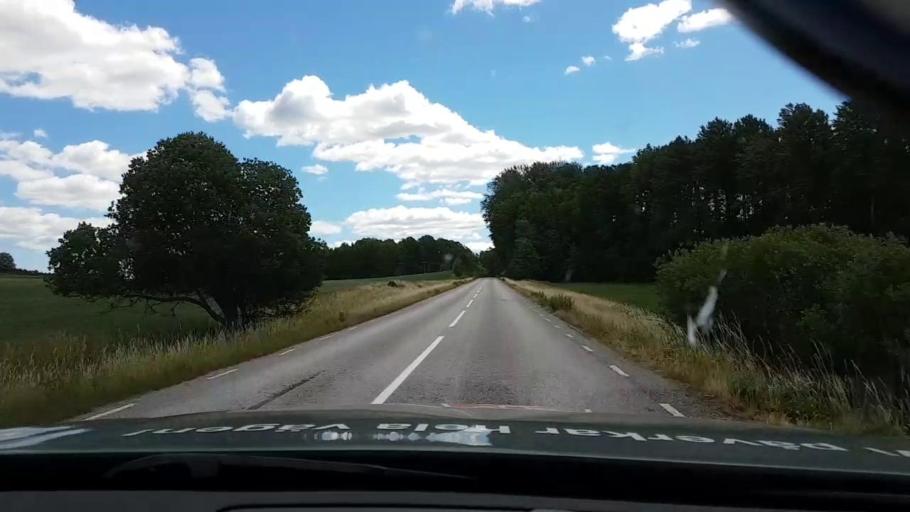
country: SE
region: Kalmar
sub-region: Vasterviks Kommun
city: Overum
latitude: 58.0628
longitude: 16.4014
